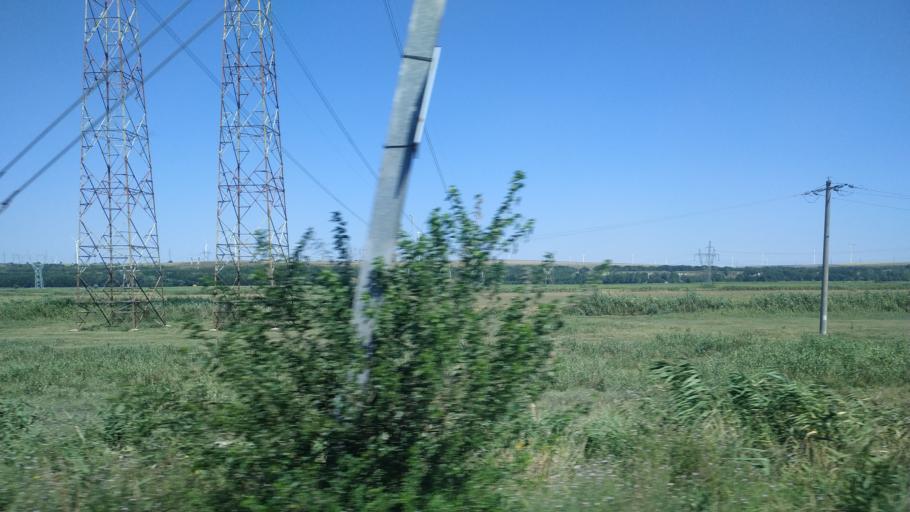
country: RO
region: Constanta
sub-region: Comuna Saligny
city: Faclia
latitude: 44.2695
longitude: 28.1231
